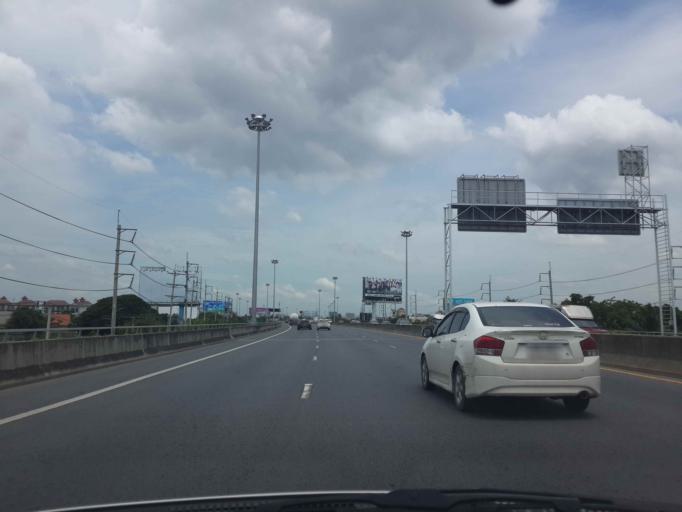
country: TH
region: Bangkok
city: Lat Phrao
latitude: 13.8331
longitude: 100.6308
